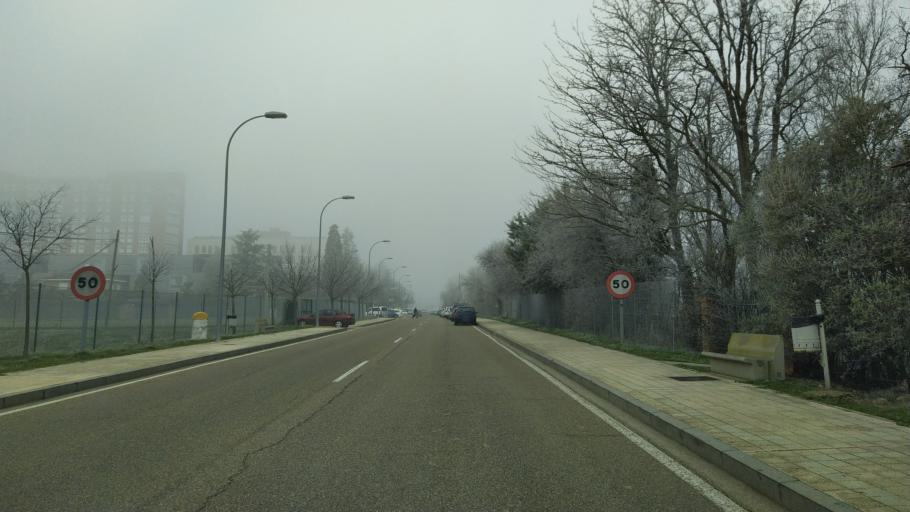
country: ES
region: Castille and Leon
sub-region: Provincia de Palencia
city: Palencia
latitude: 41.9990
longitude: -4.5380
